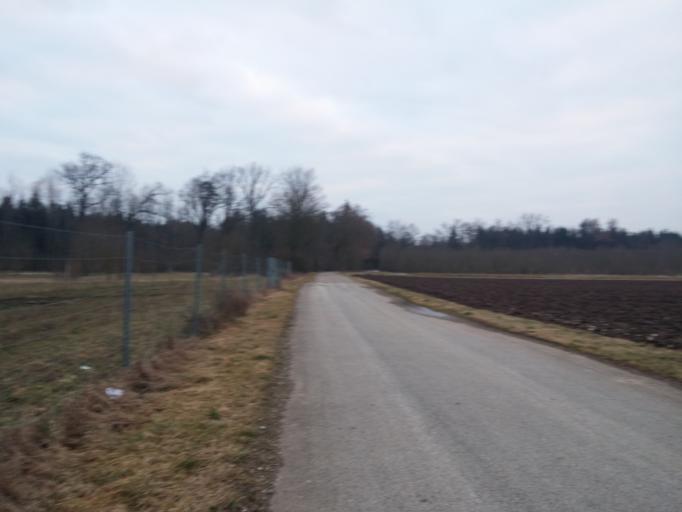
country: DE
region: Bavaria
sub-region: Upper Bavaria
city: Putzbrunn
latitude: 48.0667
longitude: 11.7199
